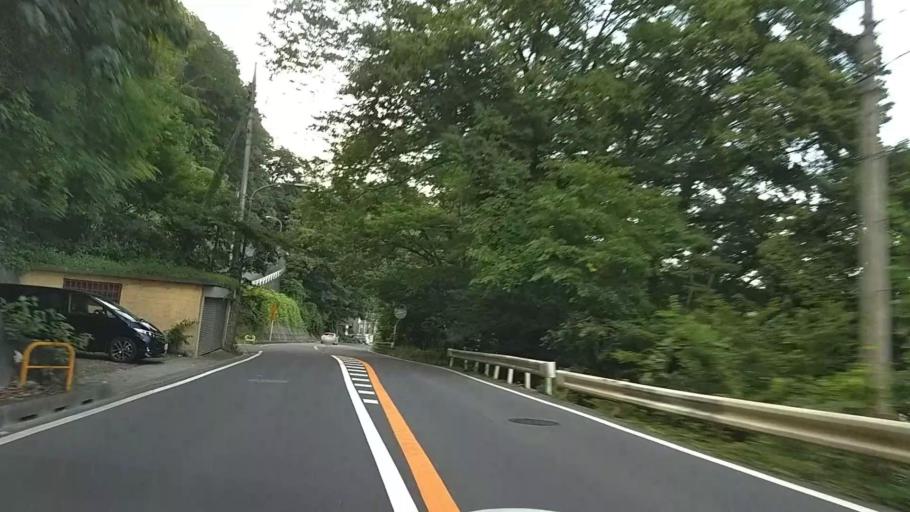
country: JP
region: Yamanashi
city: Uenohara
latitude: 35.6196
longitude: 139.1167
